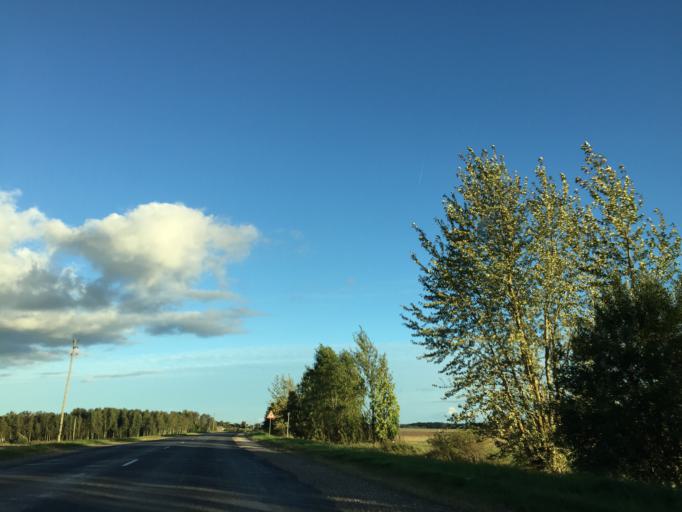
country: LV
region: Saldus Rajons
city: Saldus
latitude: 56.7055
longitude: 22.4252
